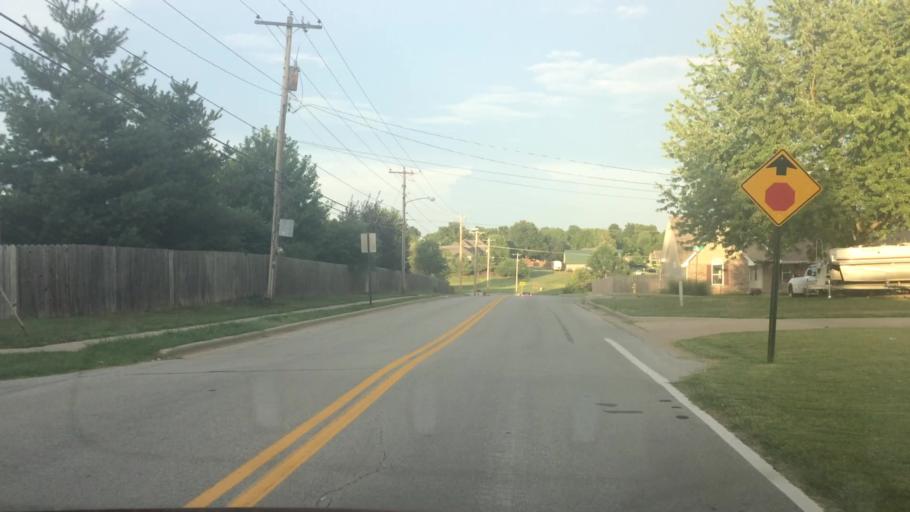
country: US
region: Missouri
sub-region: Greene County
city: Strafford
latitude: 37.2012
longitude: -93.1912
